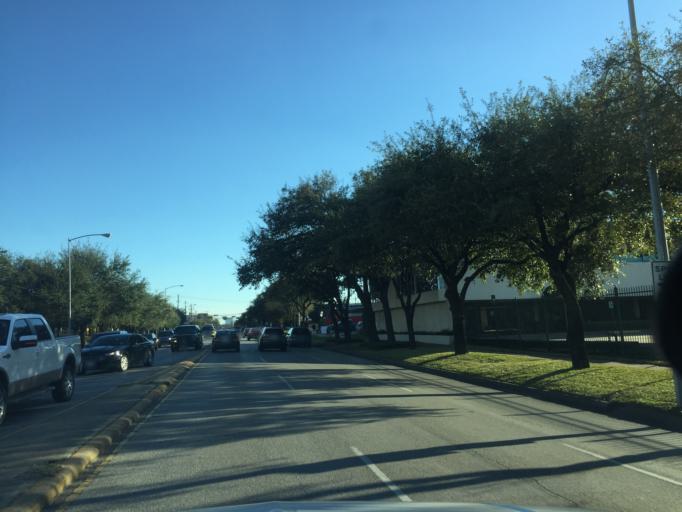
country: US
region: Texas
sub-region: Harris County
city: Houston
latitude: 29.7593
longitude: -95.3982
